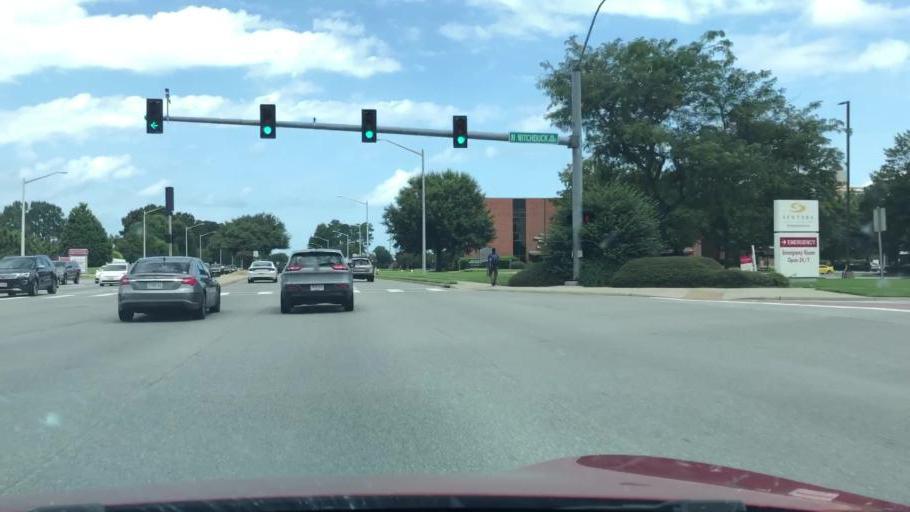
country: US
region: Virginia
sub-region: City of Chesapeake
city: Chesapeake
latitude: 36.8657
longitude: -76.1323
